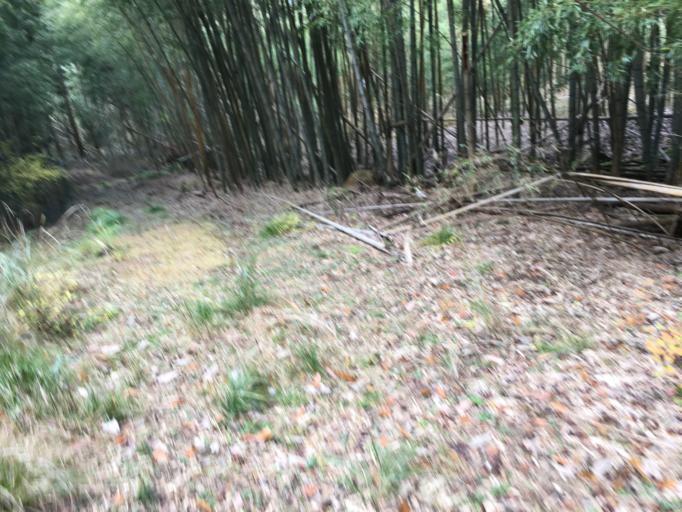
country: JP
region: Kyoto
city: Kameoka
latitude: 34.9862
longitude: 135.5533
